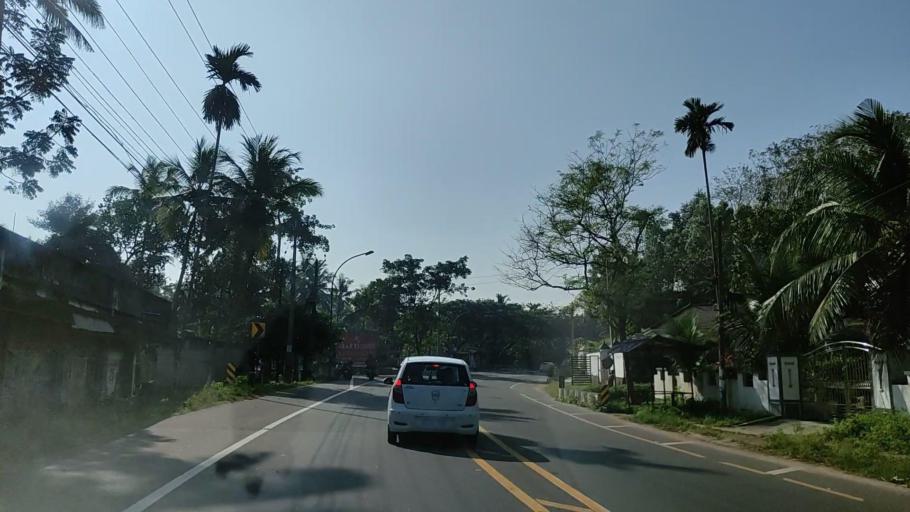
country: IN
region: Kerala
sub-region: Kollam
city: Punalur
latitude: 8.9199
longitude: 76.8553
